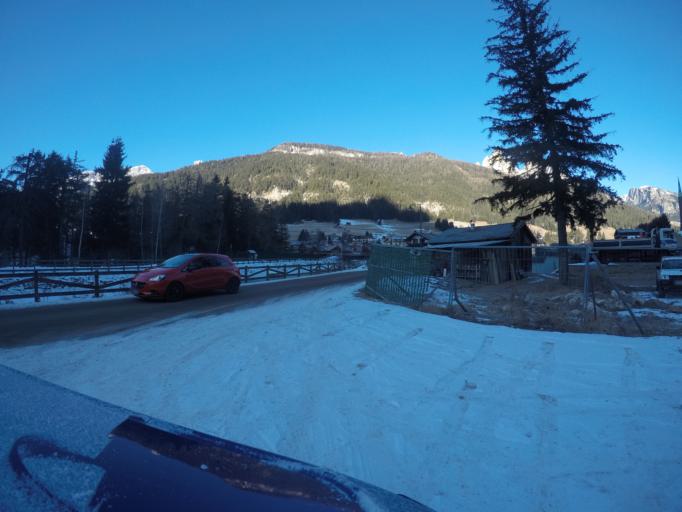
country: IT
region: Trentino-Alto Adige
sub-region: Provincia di Trento
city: Pozza di Fassa
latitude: 46.4267
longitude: 11.6874
